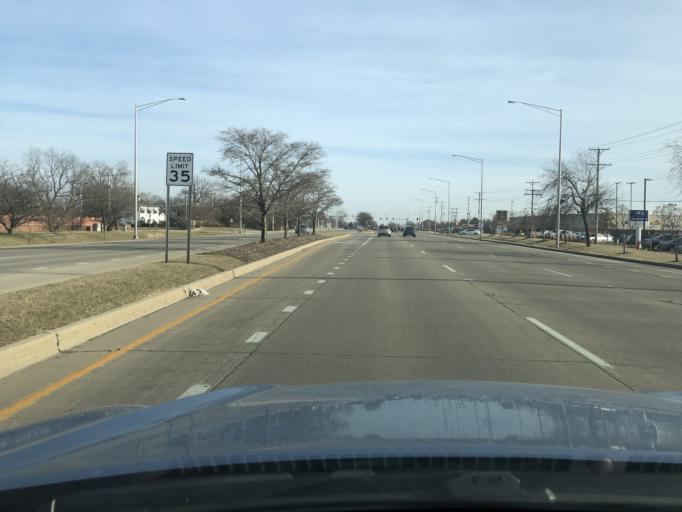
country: US
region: Illinois
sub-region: Cook County
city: Hoffman Estates
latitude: 42.0505
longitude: -88.1030
